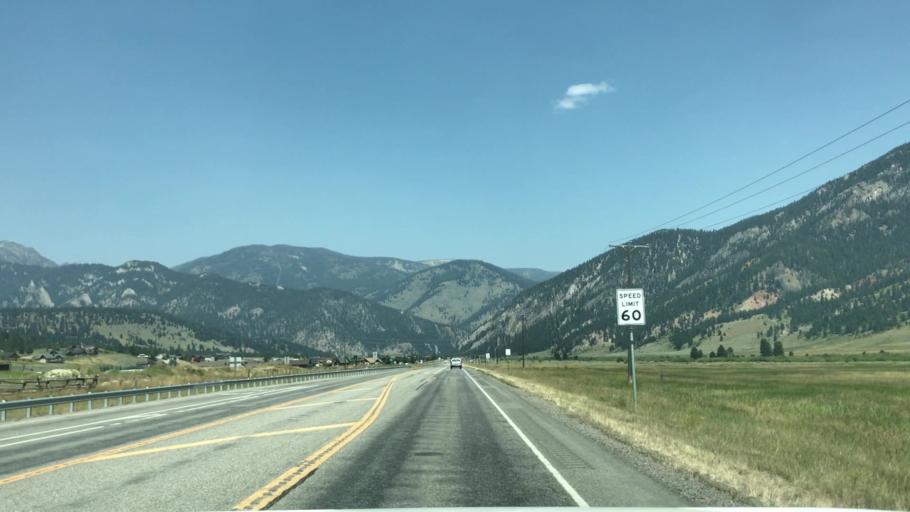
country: US
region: Montana
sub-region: Gallatin County
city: Big Sky
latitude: 45.2329
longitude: -111.2508
